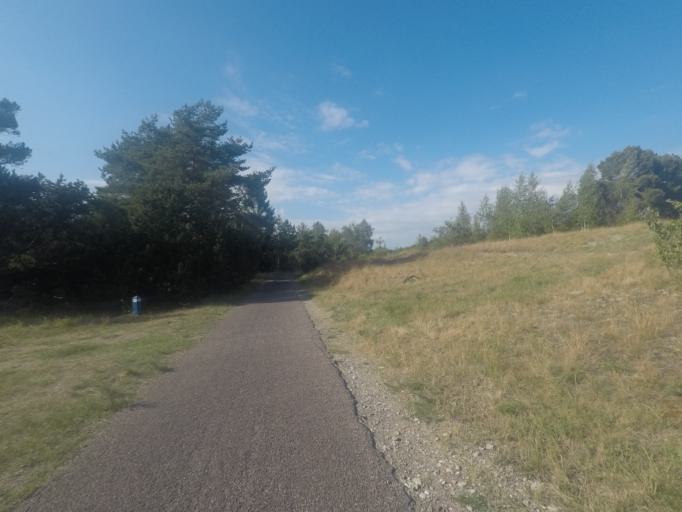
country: LT
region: Klaipedos apskritis
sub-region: Klaipeda
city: Klaipeda
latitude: 55.6020
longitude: 21.1178
